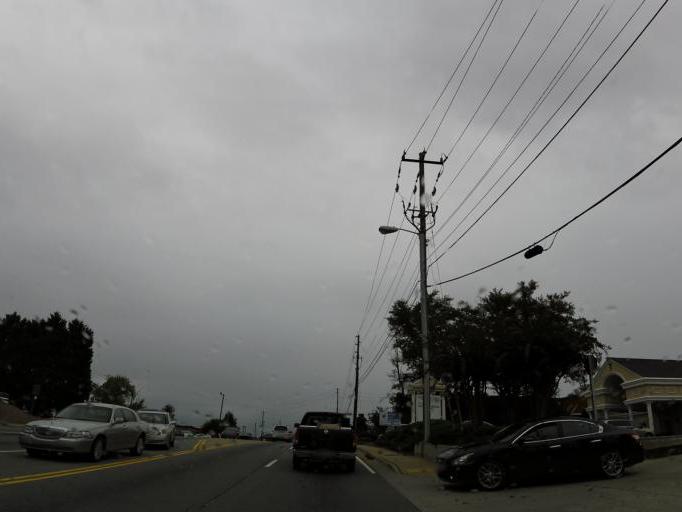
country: US
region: Georgia
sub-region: Cobb County
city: Marietta
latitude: 33.9705
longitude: -84.5505
